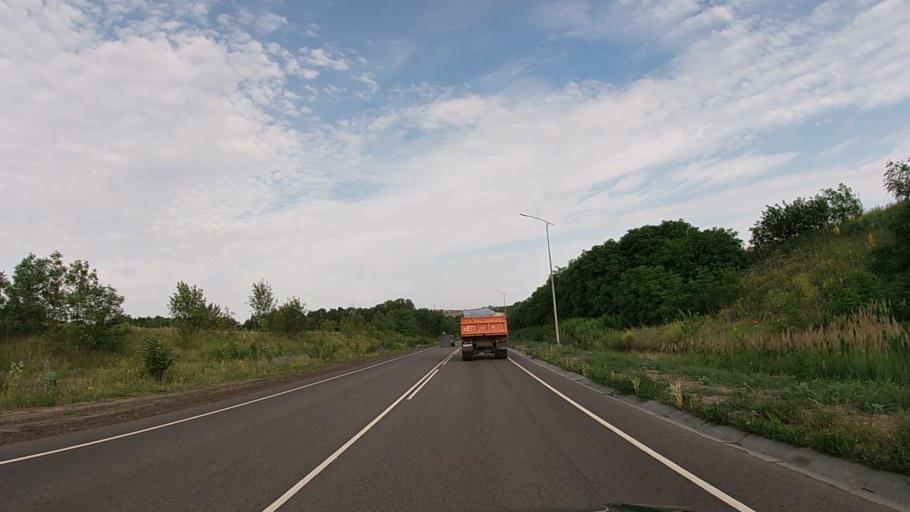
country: RU
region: Belgorod
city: Severnyy
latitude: 50.6667
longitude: 36.4949
